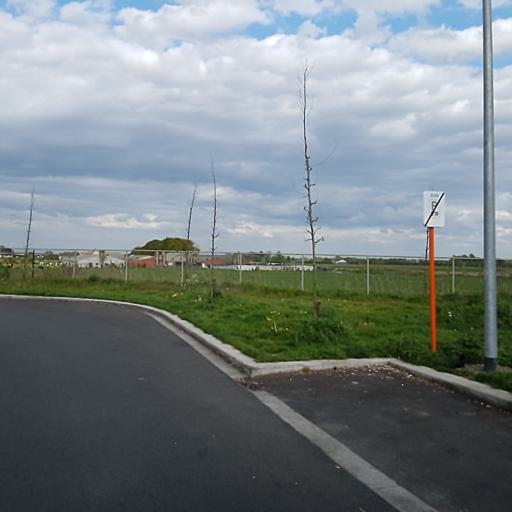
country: BE
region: Flanders
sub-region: Provincie Oost-Vlaanderen
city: Nazareth
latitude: 50.9706
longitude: 3.6100
